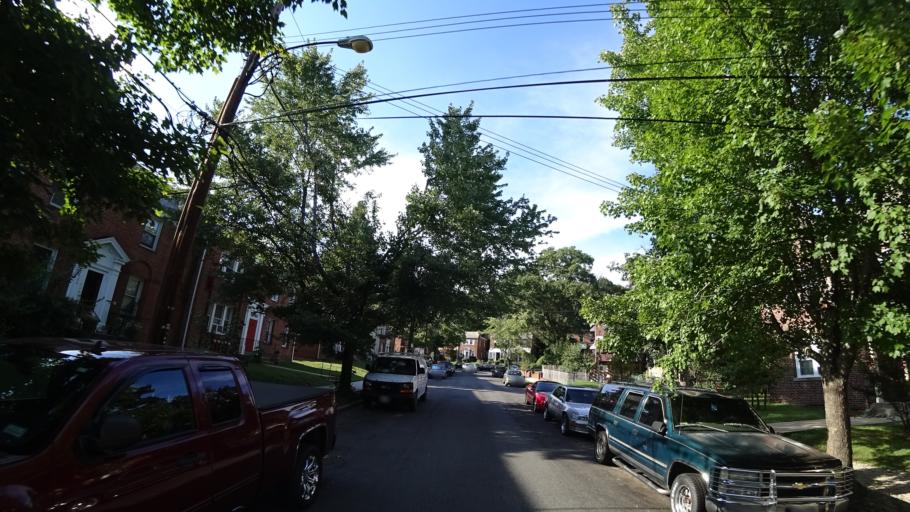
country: US
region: Maryland
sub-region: Prince George's County
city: Chillum
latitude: 38.9402
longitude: -76.9947
